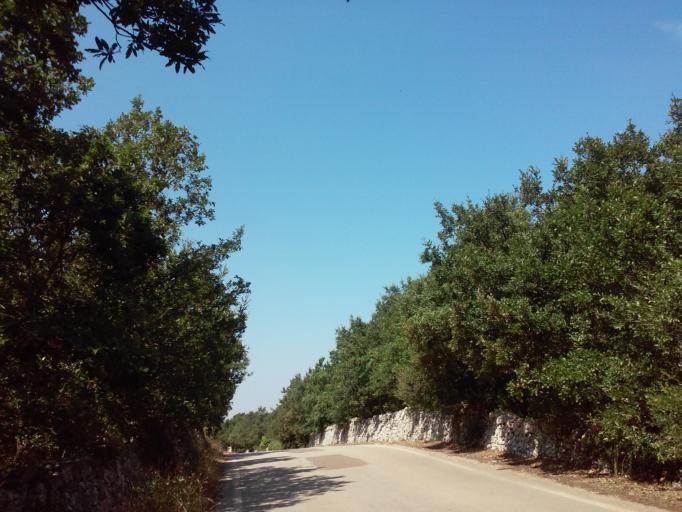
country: IT
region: Apulia
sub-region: Provincia di Bari
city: Alberobello
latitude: 40.8032
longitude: 17.2091
